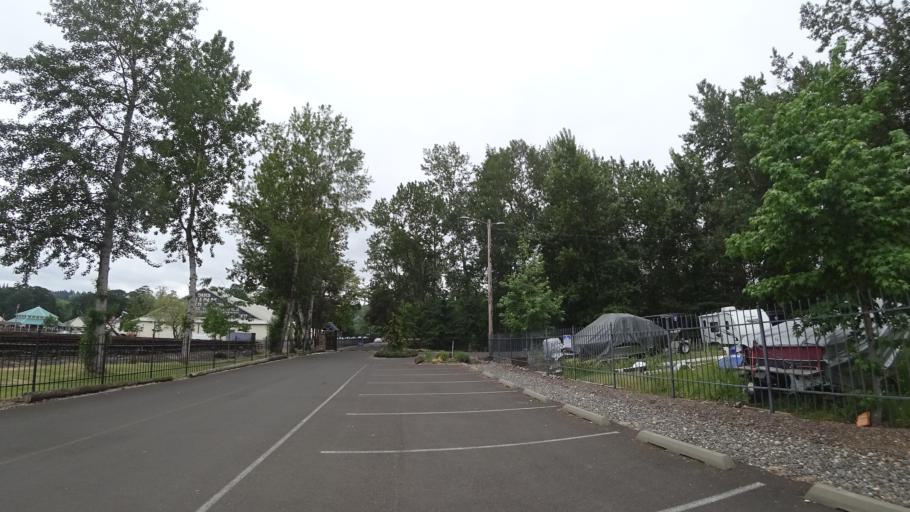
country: US
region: Oregon
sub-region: Clackamas County
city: Milwaukie
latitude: 45.4743
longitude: -122.6602
